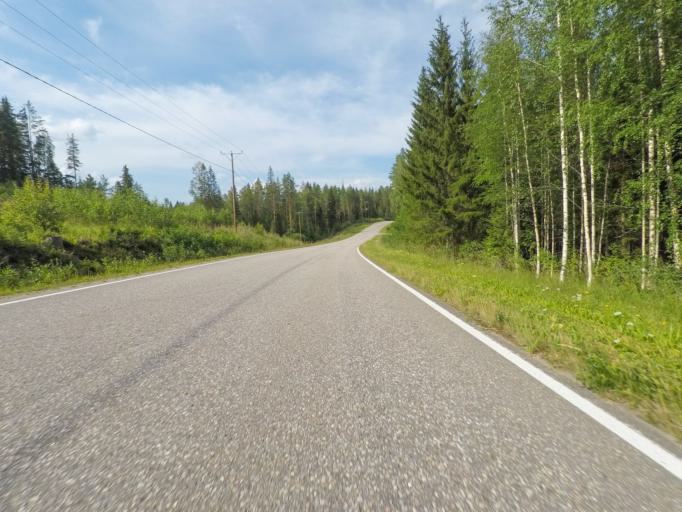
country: FI
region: Southern Savonia
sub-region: Savonlinna
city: Sulkava
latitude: 61.7783
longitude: 28.2390
